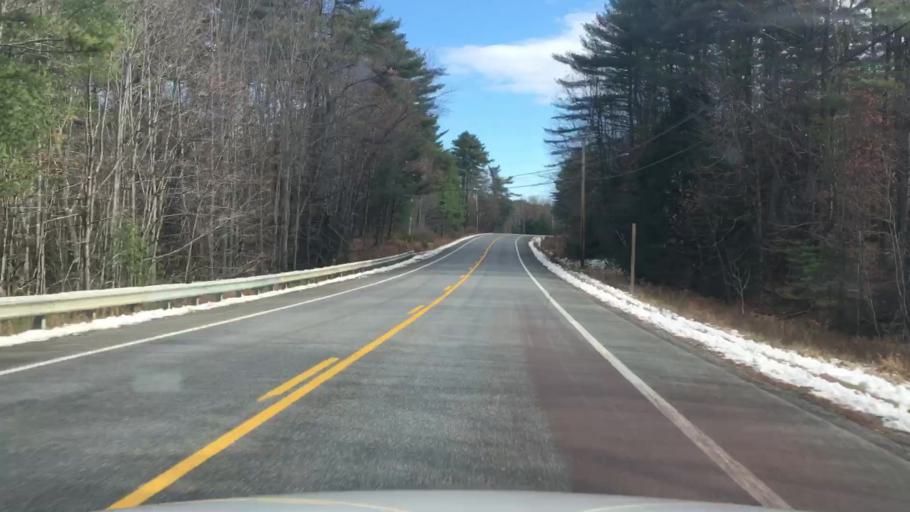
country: US
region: Maine
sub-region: Kennebec County
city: Wayne
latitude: 44.3490
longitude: -70.0537
